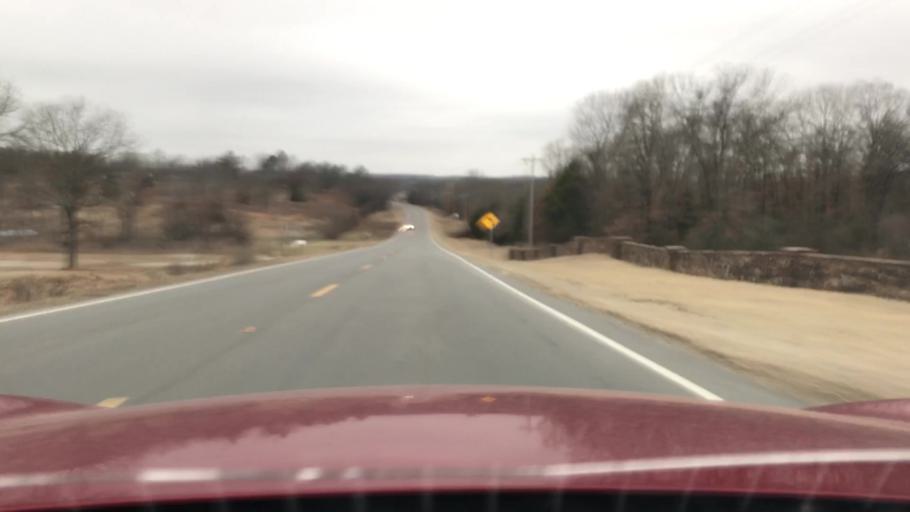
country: US
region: Oklahoma
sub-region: Sequoyah County
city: Sallisaw
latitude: 35.5169
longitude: -94.7678
